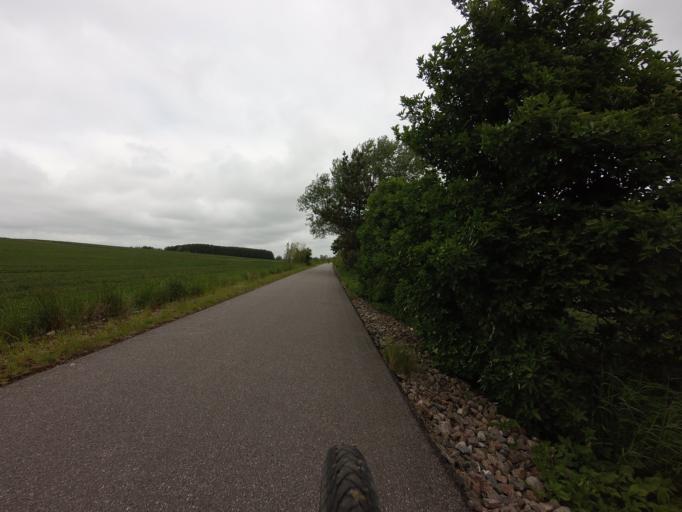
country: DK
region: Zealand
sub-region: Slagelse Kommune
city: Slagelse
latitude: 55.3352
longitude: 11.3955
